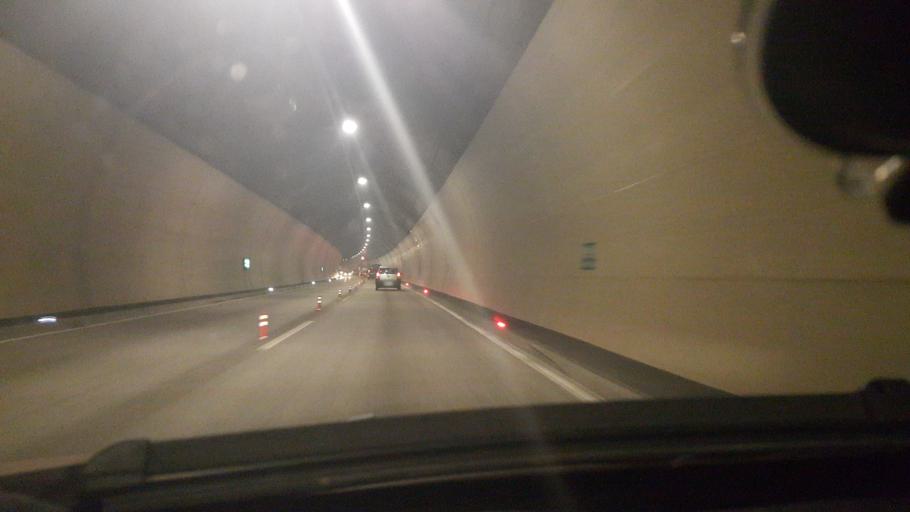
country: AT
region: Carinthia
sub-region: Klagenfurt am Woerthersee
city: Klagenfurt am Woerthersee
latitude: 46.6564
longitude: 14.3005
